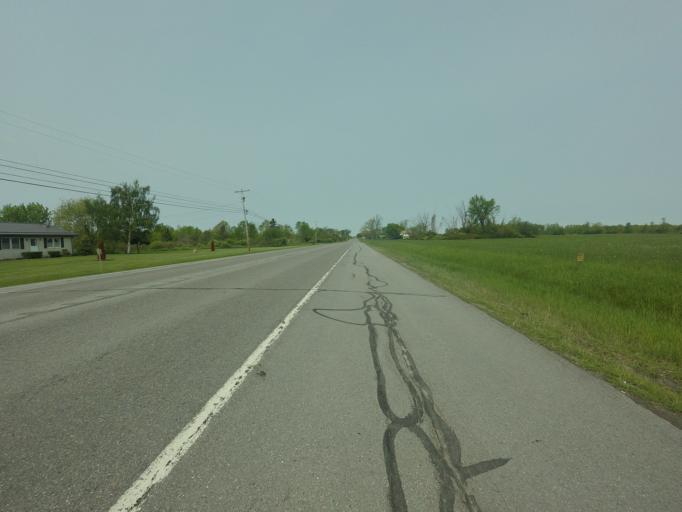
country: US
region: New York
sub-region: Jefferson County
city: Dexter
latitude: 44.0339
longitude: -76.0599
